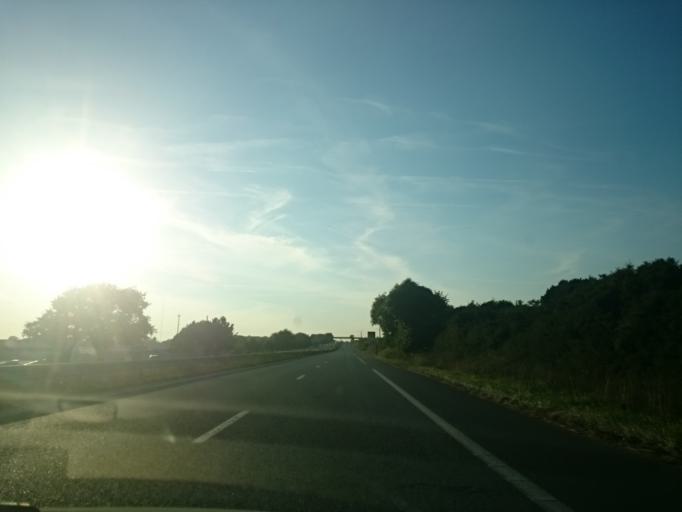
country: FR
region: Brittany
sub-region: Departement du Morbihan
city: Theix
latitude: 47.6338
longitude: -2.6585
